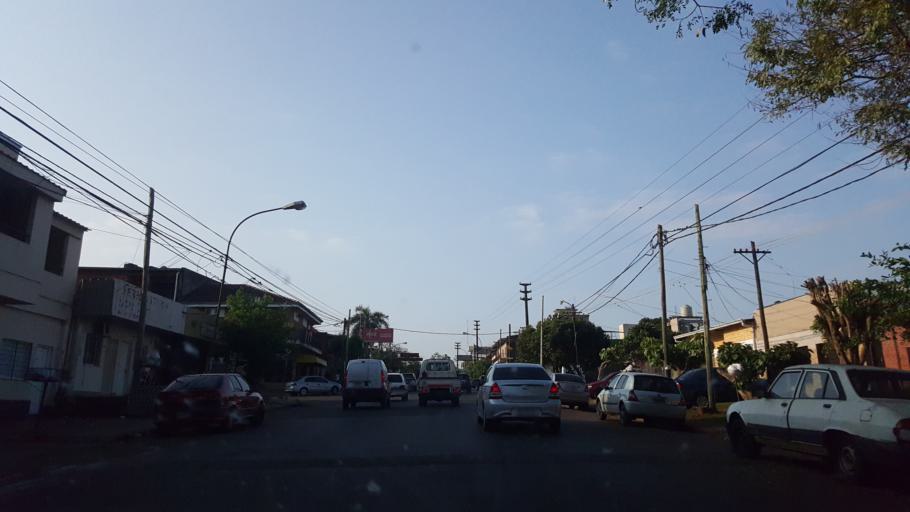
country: AR
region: Misiones
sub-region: Departamento de Capital
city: Posadas
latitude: -27.3902
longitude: -55.8970
